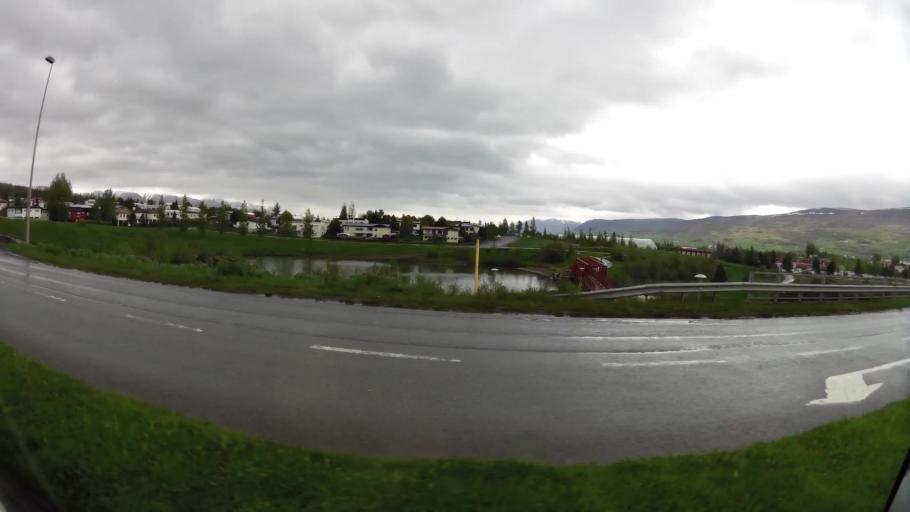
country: IS
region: Northeast
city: Akureyri
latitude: 65.6870
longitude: -18.1209
